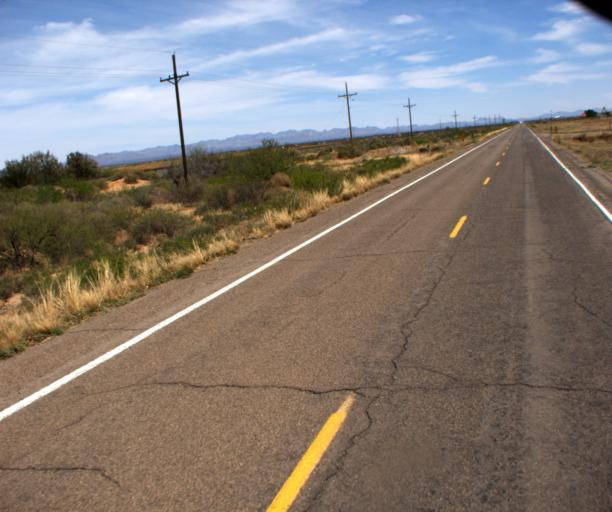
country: US
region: Arizona
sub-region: Cochise County
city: Willcox
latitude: 32.3234
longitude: -109.4661
